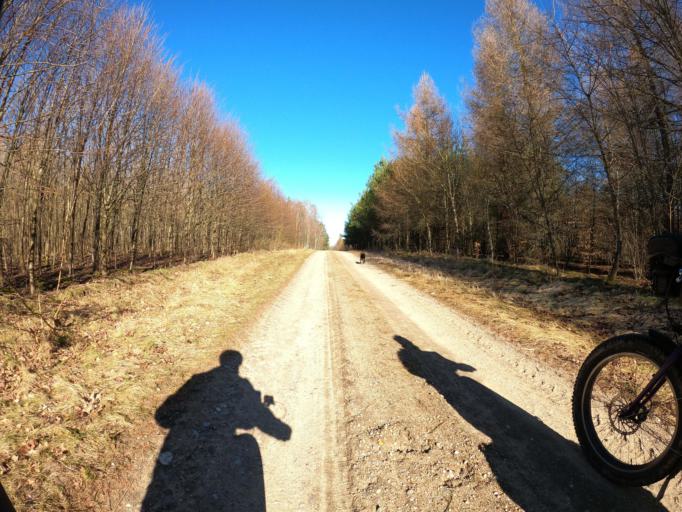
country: PL
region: Greater Poland Voivodeship
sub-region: Powiat zlotowski
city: Sypniewo
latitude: 53.4912
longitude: 16.6405
